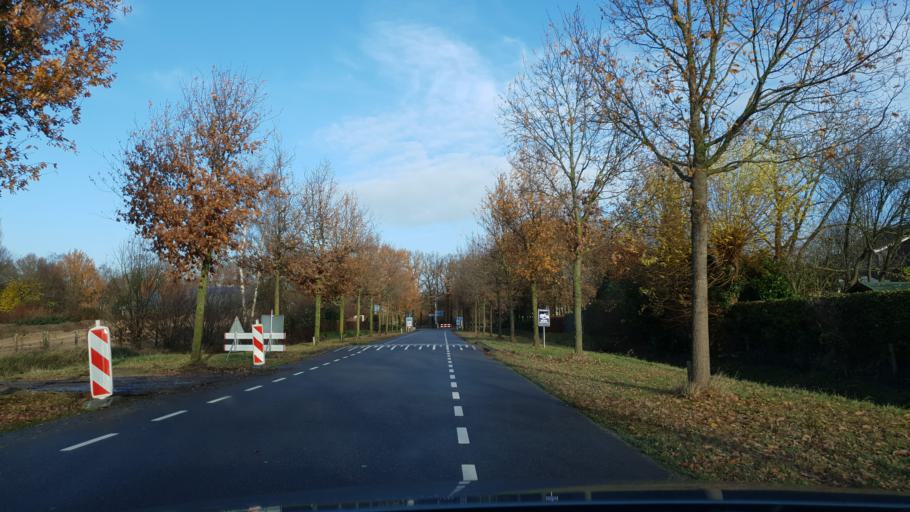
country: NL
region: Gelderland
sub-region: Gemeente Wijchen
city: Bergharen
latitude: 51.8326
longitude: 5.6788
